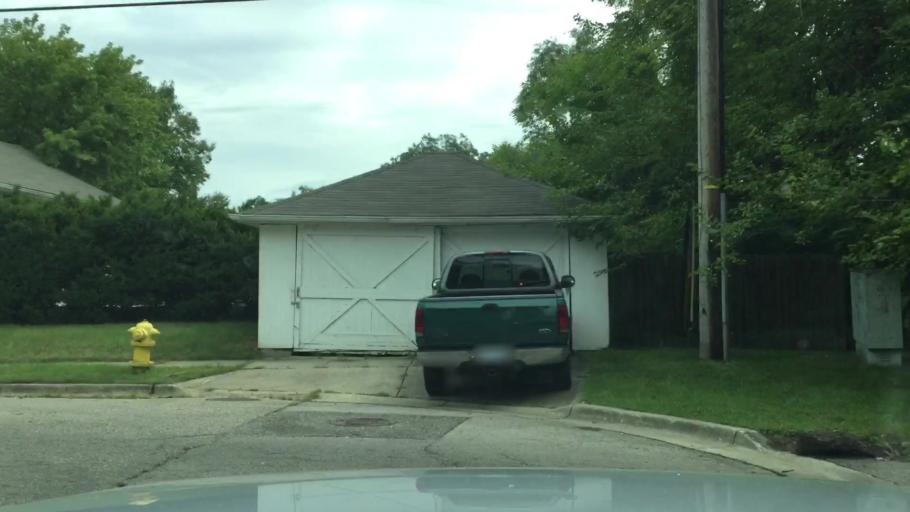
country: US
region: Michigan
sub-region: Oakland County
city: Sylvan Lake
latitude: 42.6267
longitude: -83.3226
